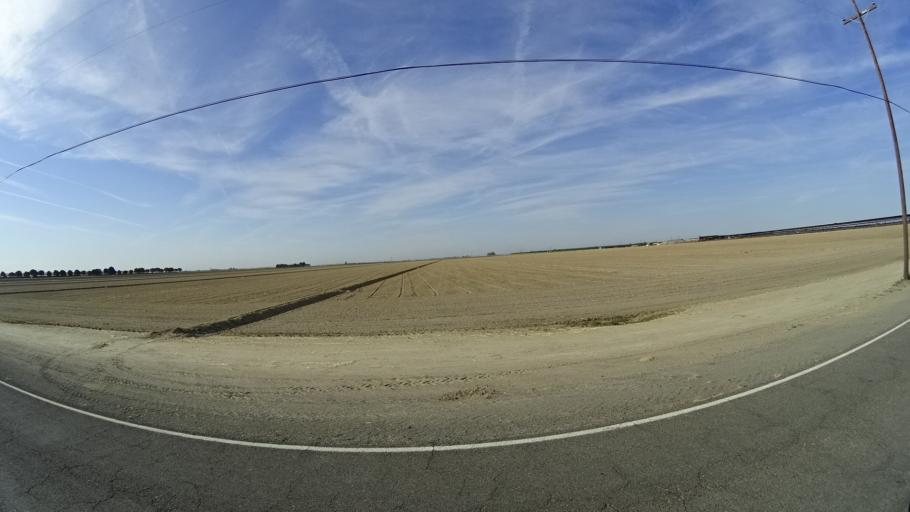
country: US
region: California
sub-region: Fresno County
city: Kingsburg
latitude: 36.4013
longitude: -119.5343
